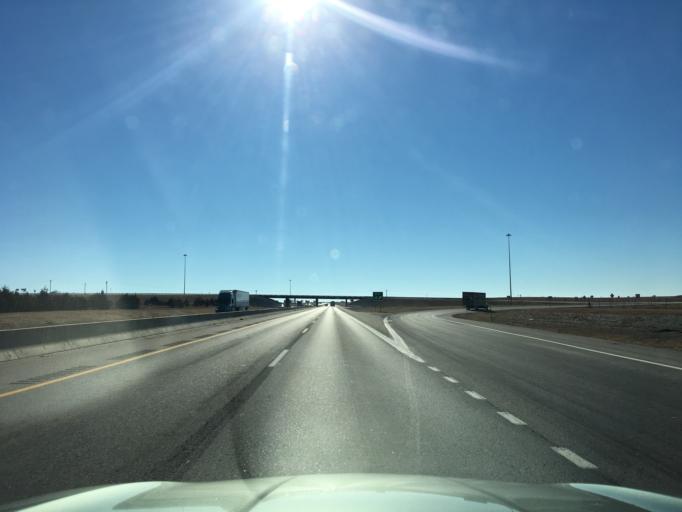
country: US
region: Kansas
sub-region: Sumner County
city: Wellington
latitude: 37.0607
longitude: -97.3385
